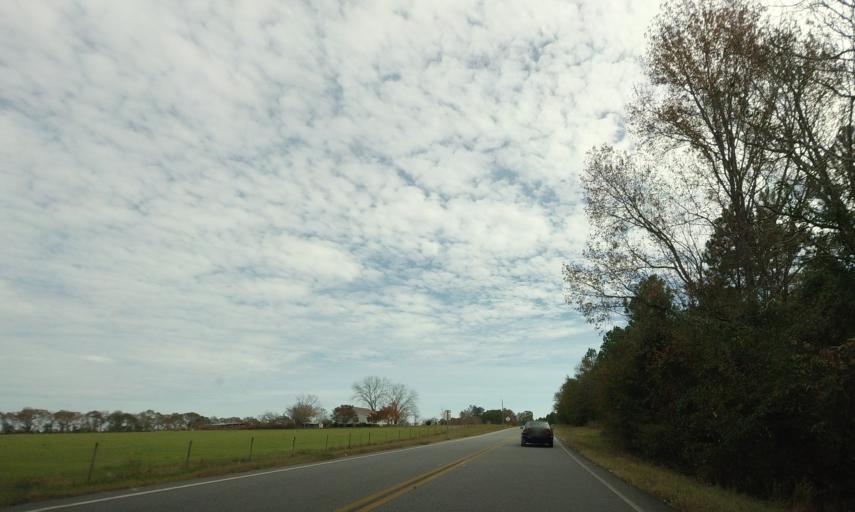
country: US
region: Georgia
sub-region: Dodge County
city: Chester
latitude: 32.4099
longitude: -83.2282
